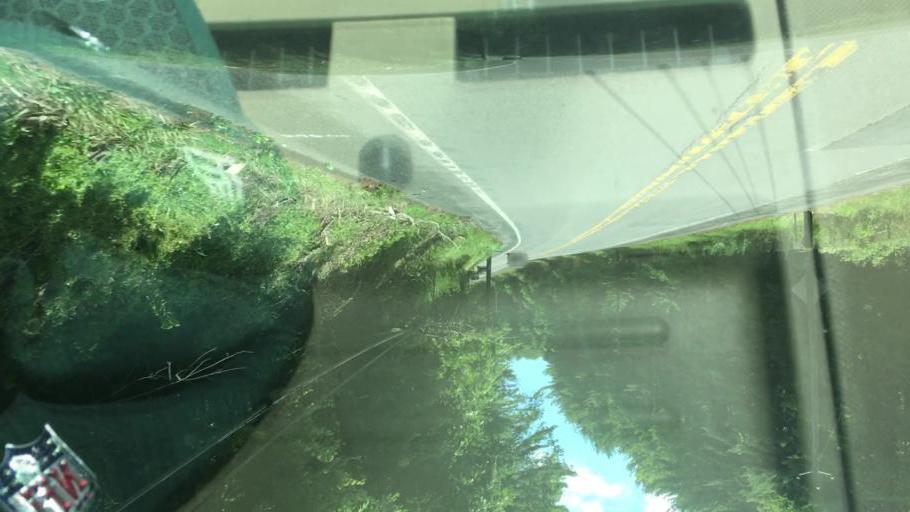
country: US
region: Pennsylvania
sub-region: Schuylkill County
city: Minersville
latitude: 40.6913
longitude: -76.2742
